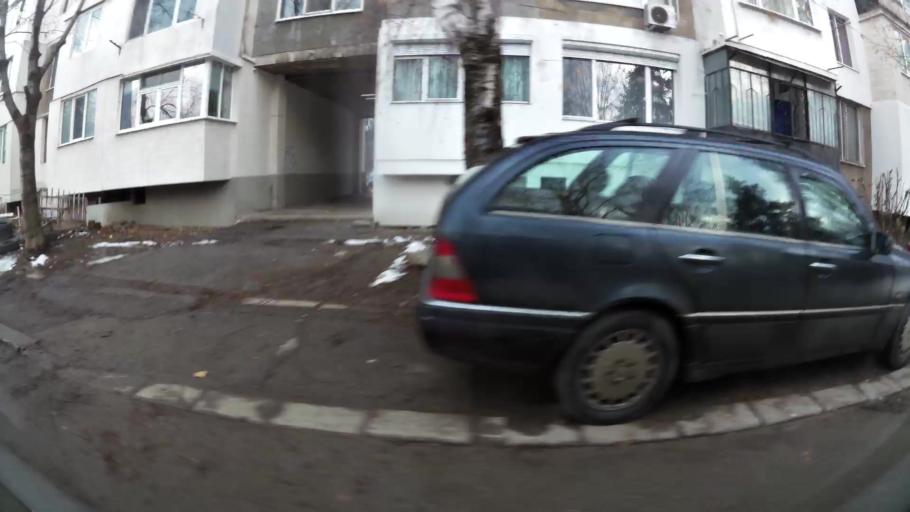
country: BG
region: Sofia-Capital
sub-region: Stolichna Obshtina
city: Sofia
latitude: 42.6903
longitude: 23.2855
